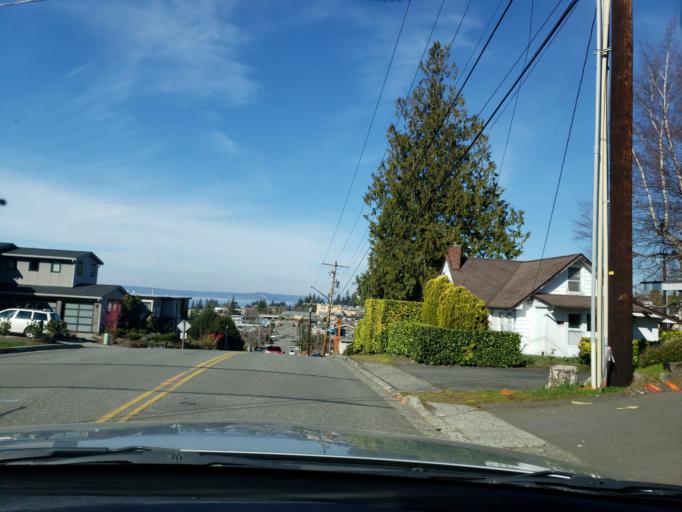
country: US
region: Washington
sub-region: Snohomish County
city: Edmonds
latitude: 47.8060
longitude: -122.3722
